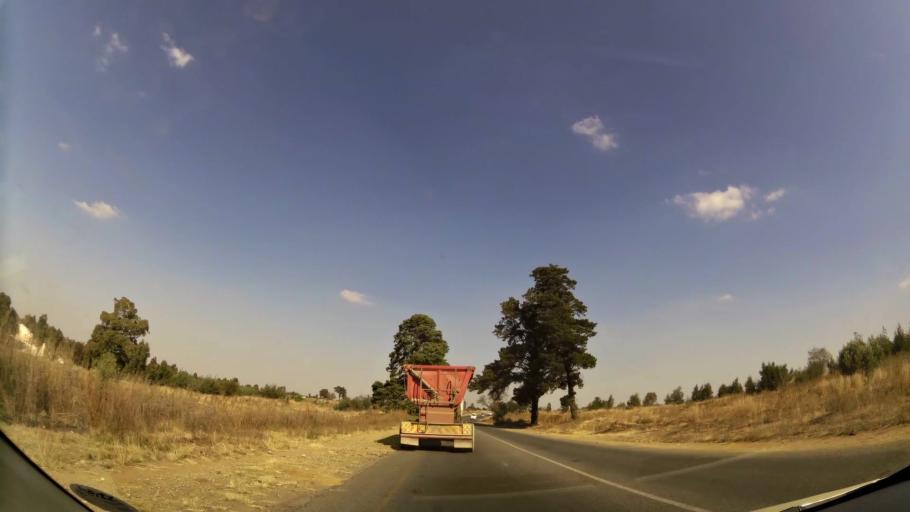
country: ZA
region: Gauteng
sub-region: West Rand District Municipality
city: Krugersdorp
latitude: -26.1270
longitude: 27.8144
